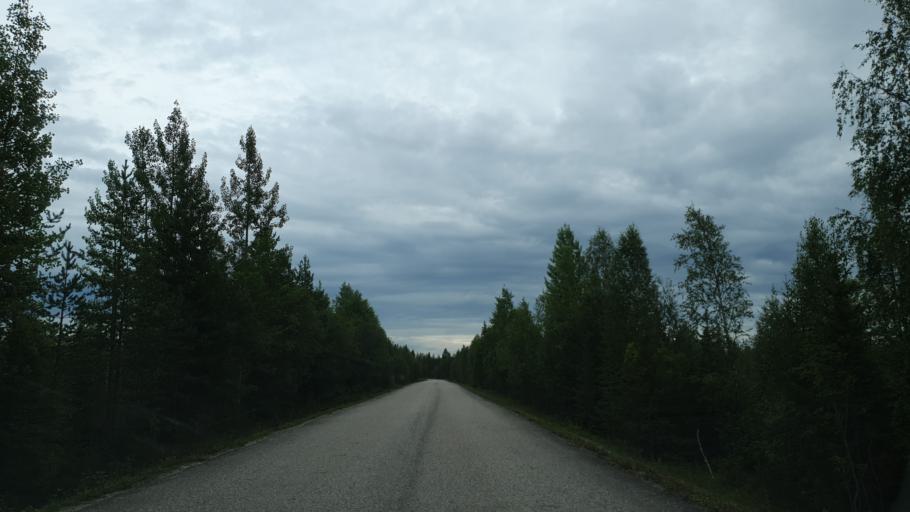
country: FI
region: Kainuu
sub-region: Kehys-Kainuu
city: Kuhmo
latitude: 64.3507
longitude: 29.1280
